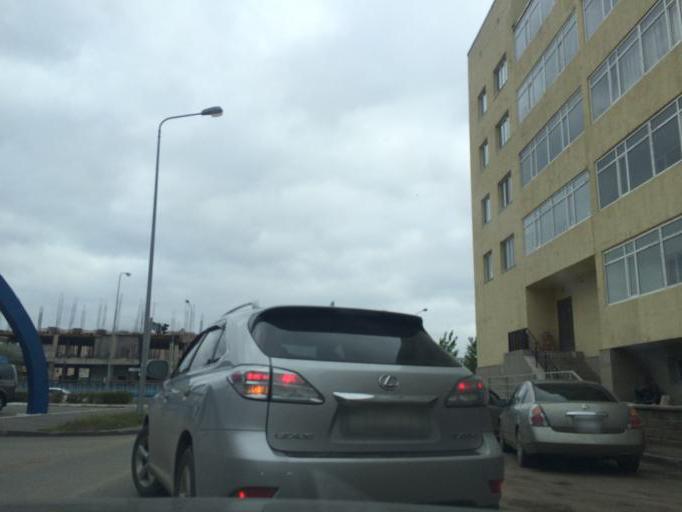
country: KZ
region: Astana Qalasy
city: Astana
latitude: 51.1463
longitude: 71.4768
